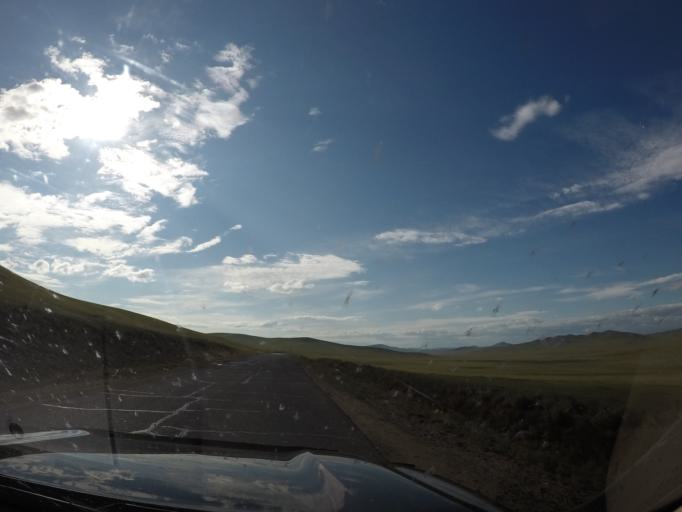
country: MN
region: Hentiy
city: Modot
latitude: 47.8096
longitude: 108.7968
